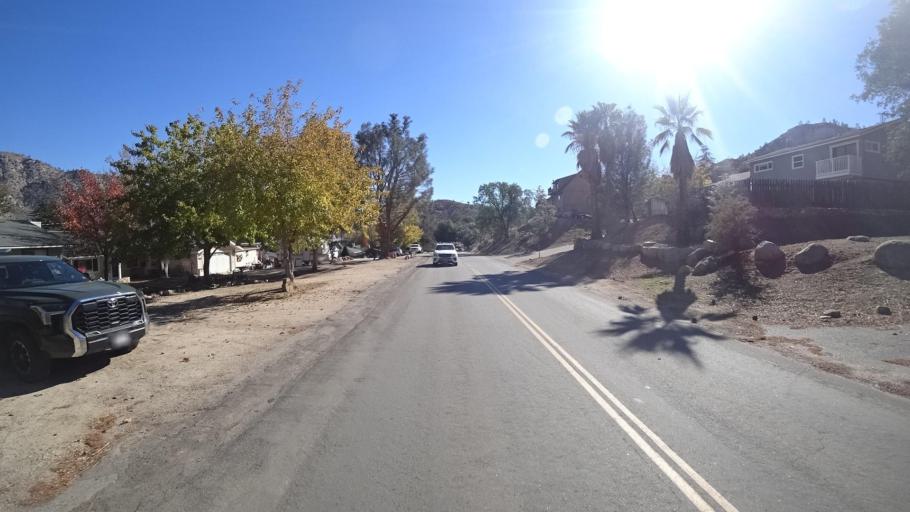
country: US
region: California
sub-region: Kern County
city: Kernville
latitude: 35.7598
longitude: -118.4309
